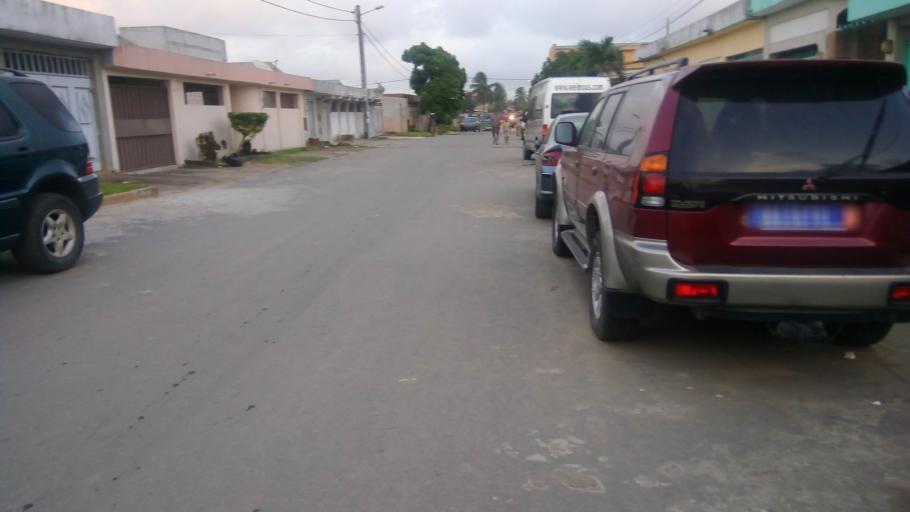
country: CI
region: Lagunes
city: Abobo
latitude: 5.4086
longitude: -3.9894
